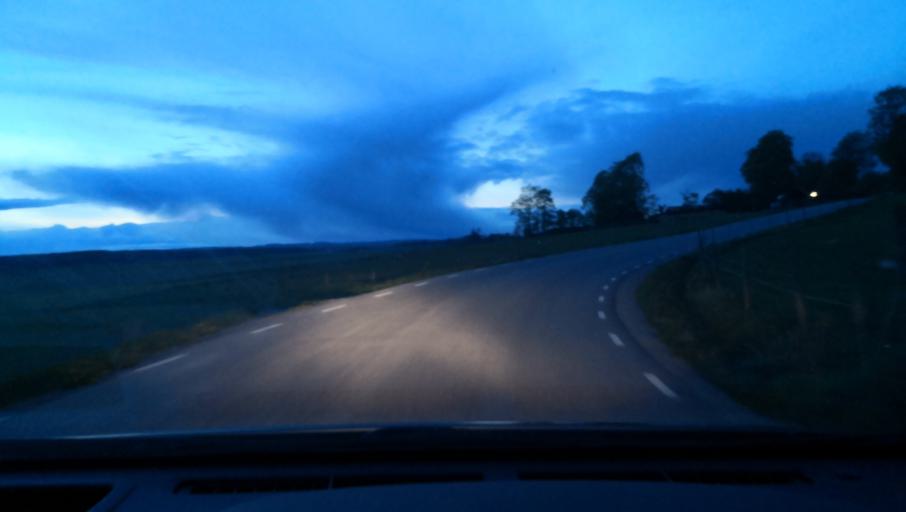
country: SE
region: OErebro
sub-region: Orebro Kommun
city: Vintrosa
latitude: 59.1602
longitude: 15.0006
